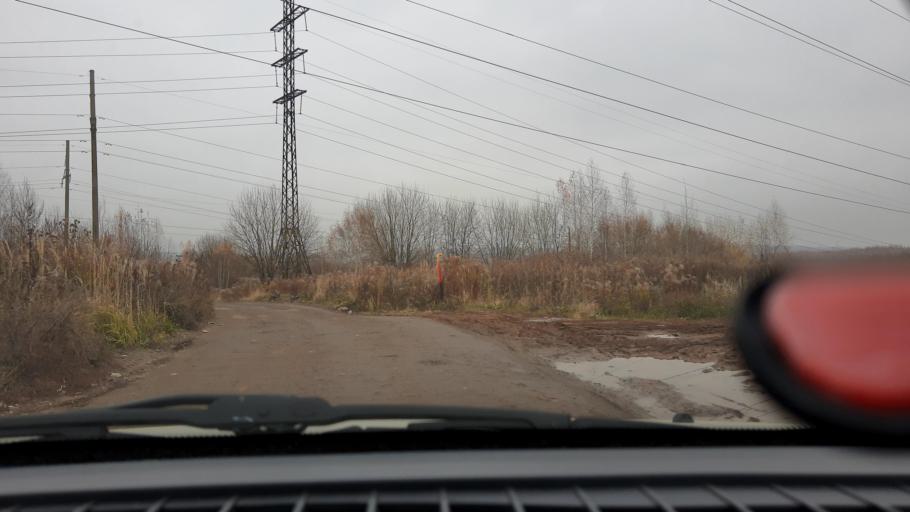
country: RU
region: Nizjnij Novgorod
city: Afonino
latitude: 56.2544
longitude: 44.0493
